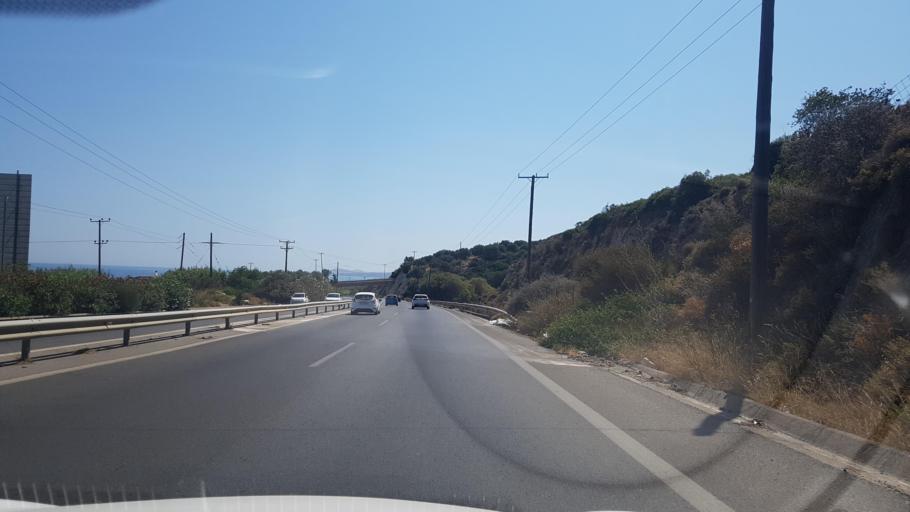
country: GR
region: Crete
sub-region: Nomos Rethymnis
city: Rethymno
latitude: 35.3600
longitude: 24.4914
